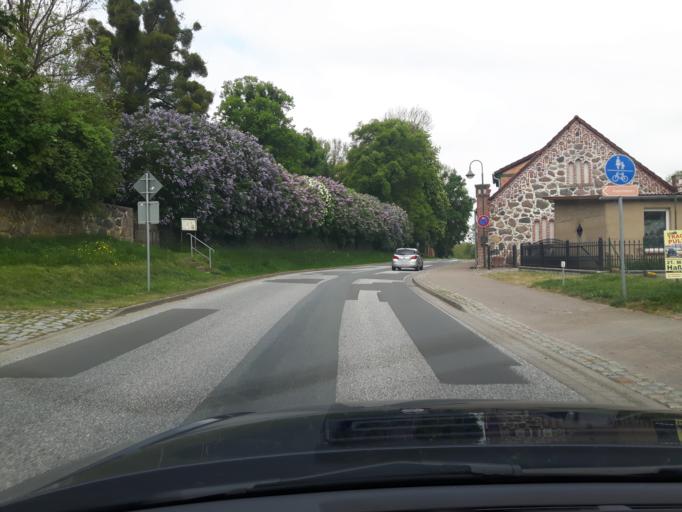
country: DE
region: Mecklenburg-Vorpommern
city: Gross Wokern
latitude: 53.6509
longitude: 12.4997
